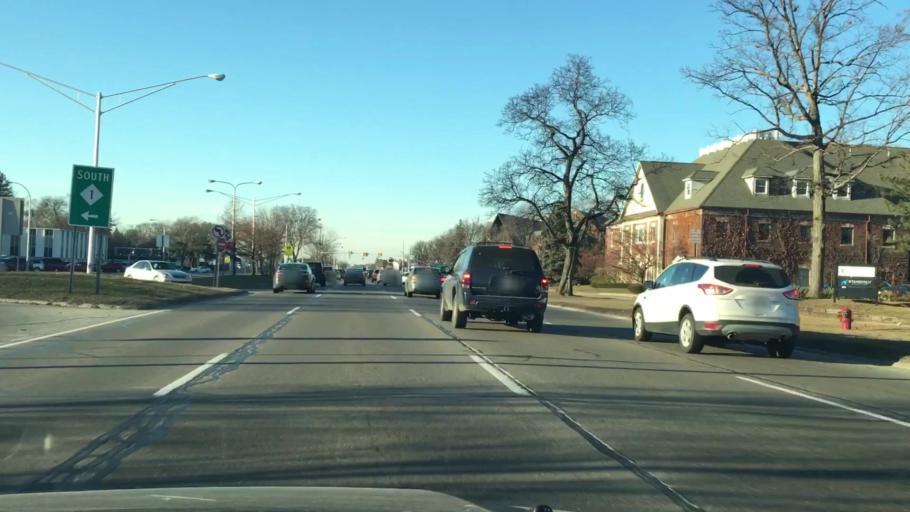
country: US
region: Michigan
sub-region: Oakland County
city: Royal Oak
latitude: 42.4873
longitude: -83.1565
